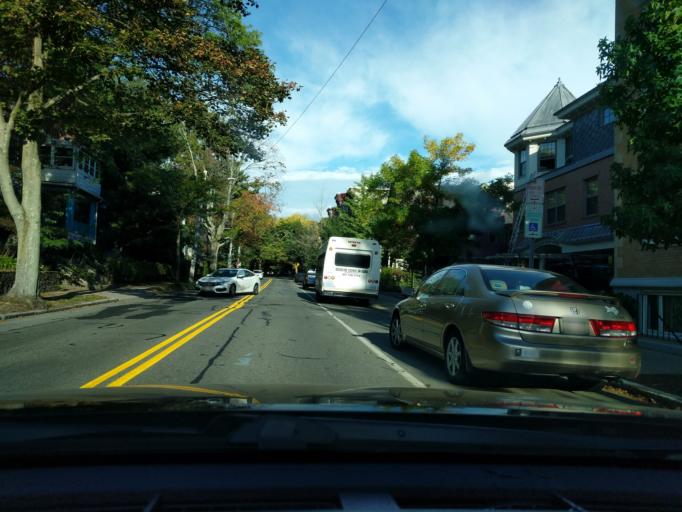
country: US
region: Massachusetts
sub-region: Norfolk County
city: Brookline
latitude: 42.3433
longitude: -71.1277
